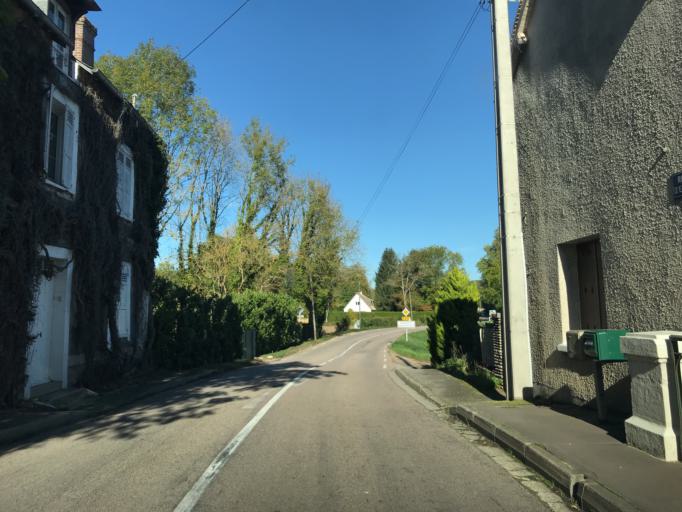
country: FR
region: Haute-Normandie
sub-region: Departement de l'Eure
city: Saint-Aubin-sur-Gaillon
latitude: 49.0887
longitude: 1.2679
